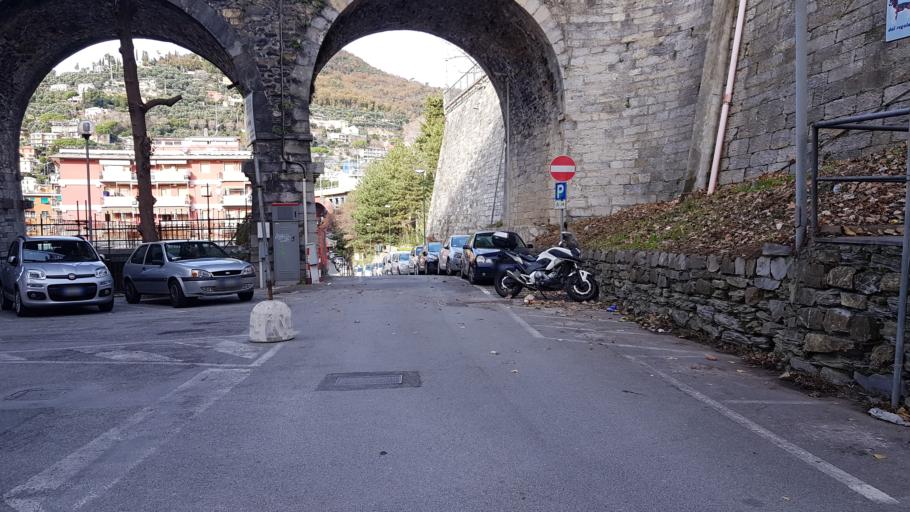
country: IT
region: Liguria
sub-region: Provincia di Genova
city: Recco
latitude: 44.3606
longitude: 9.1463
